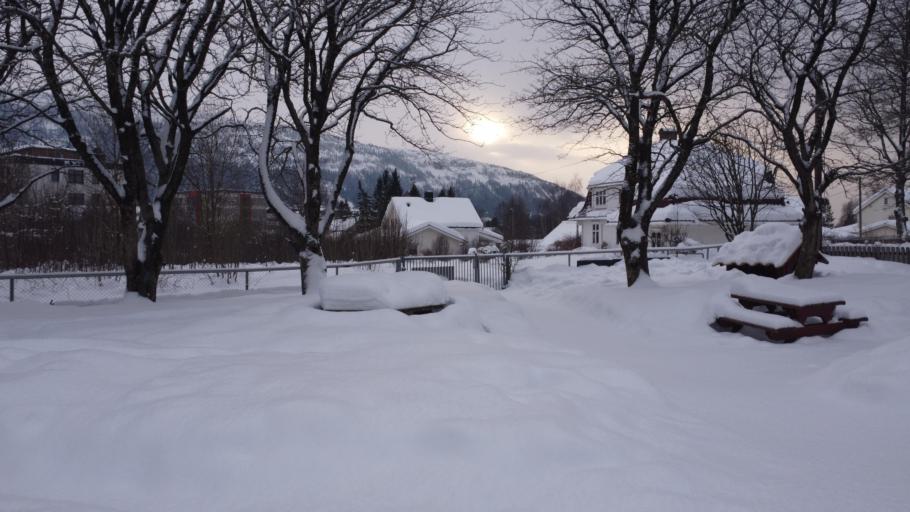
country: NO
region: Nordland
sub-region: Rana
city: Mo i Rana
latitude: 66.3135
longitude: 14.1464
